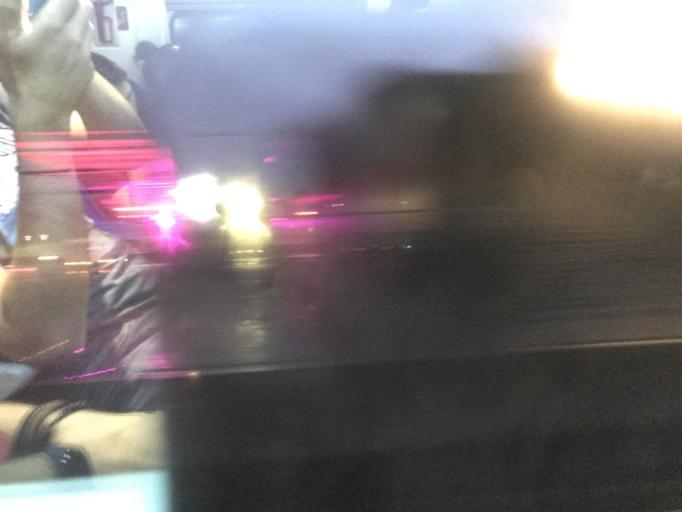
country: TR
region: Kocaeli
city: Izmit
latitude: 40.7605
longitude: 29.9080
